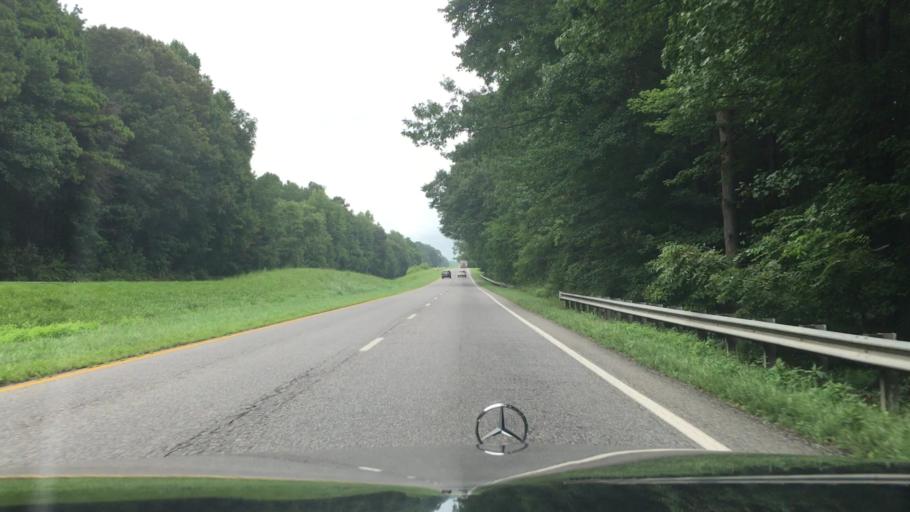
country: US
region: Virginia
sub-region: Amelia County
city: Amelia Court House
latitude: 37.3229
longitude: -78.0342
